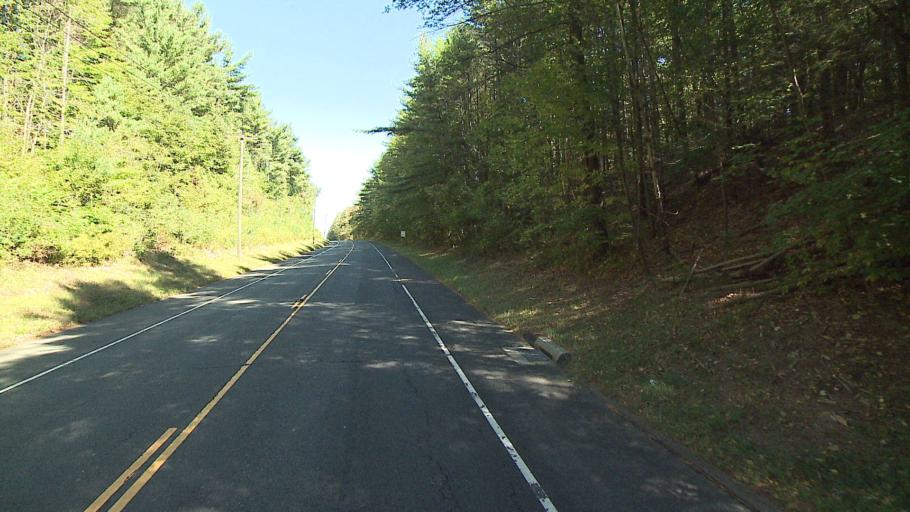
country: US
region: Connecticut
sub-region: Hartford County
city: Collinsville
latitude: 41.8249
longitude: -72.9479
